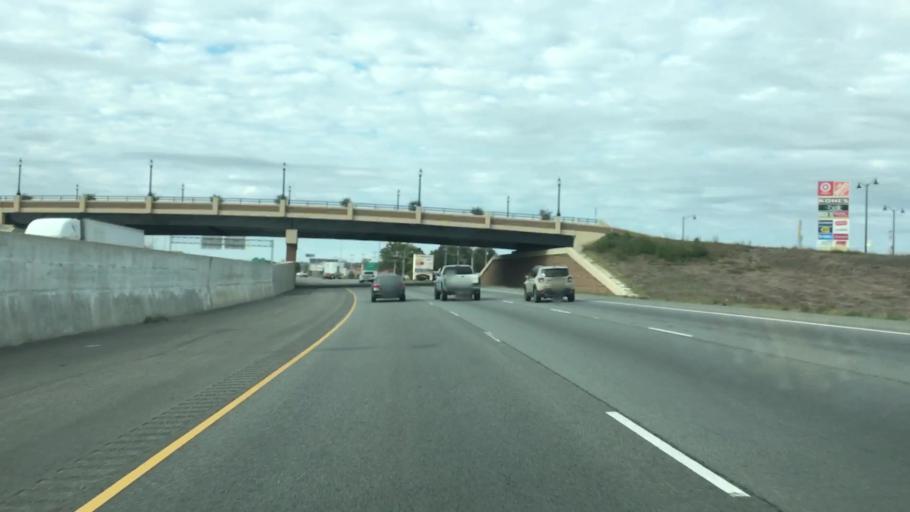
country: US
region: Arkansas
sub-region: Faulkner County
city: Conway
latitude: 35.0836
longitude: -92.4146
